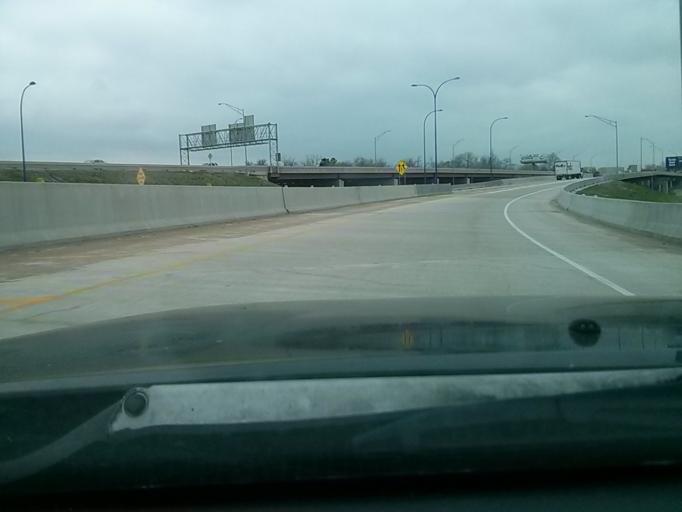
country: US
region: Oklahoma
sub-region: Tulsa County
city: Tulsa
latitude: 36.1466
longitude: -96.0016
